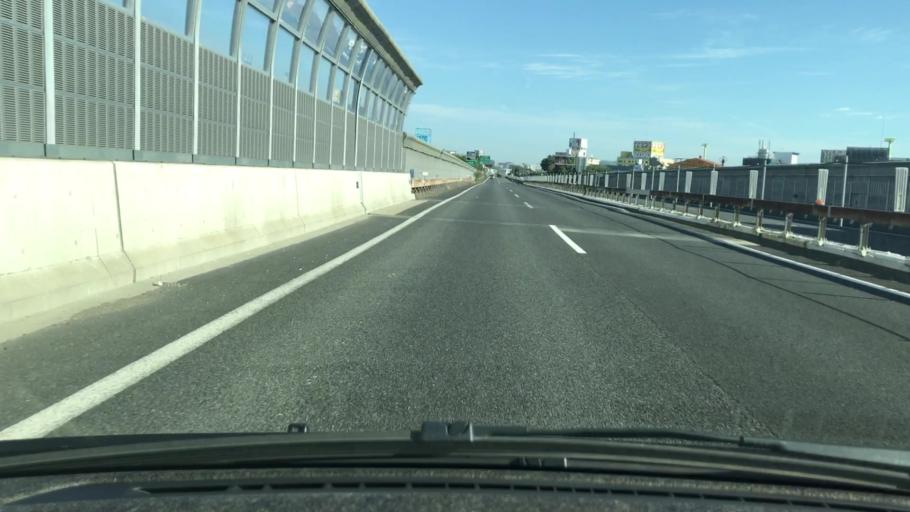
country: JP
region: Osaka
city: Toyonaka
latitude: 34.7490
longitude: 135.4569
